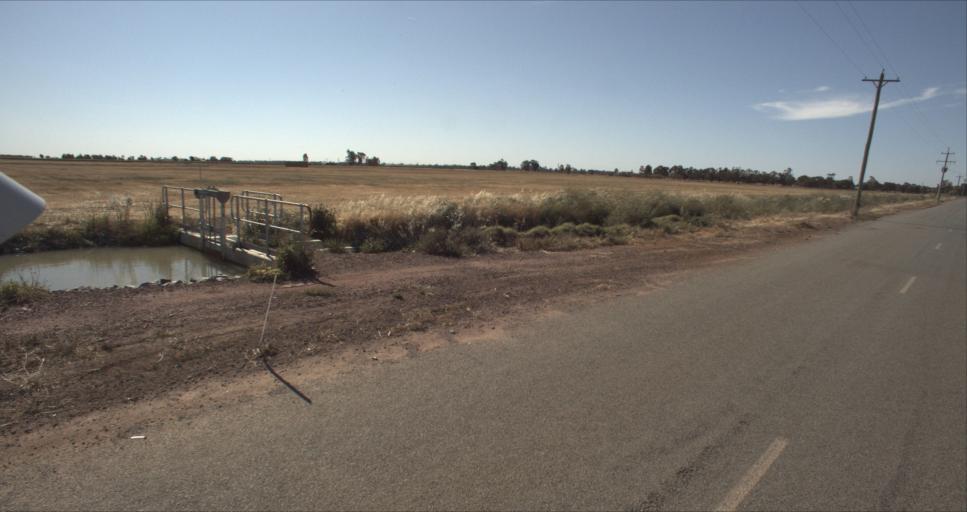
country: AU
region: New South Wales
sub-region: Leeton
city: Leeton
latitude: -34.5753
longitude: 146.3809
